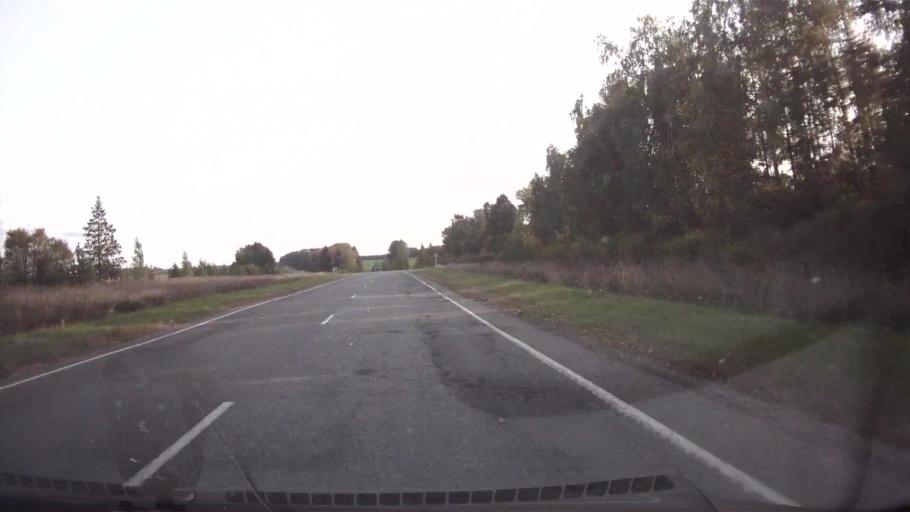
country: RU
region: Mariy-El
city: Kuzhener
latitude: 56.8906
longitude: 48.7517
